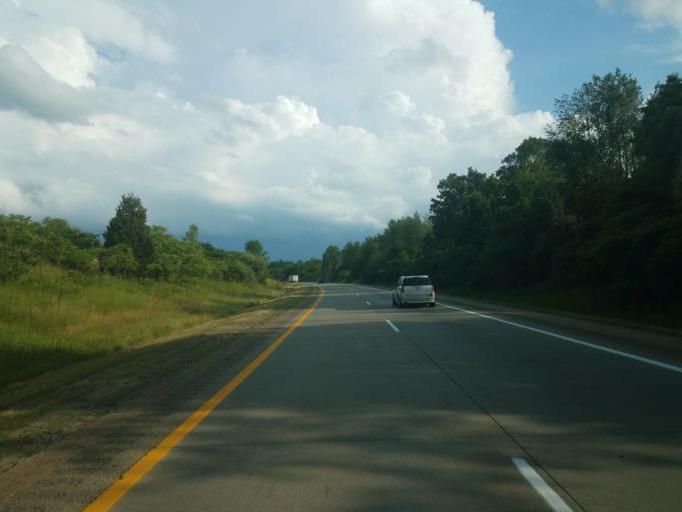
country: US
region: Michigan
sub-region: Calhoun County
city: Marshall
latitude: 42.1590
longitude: -84.9938
